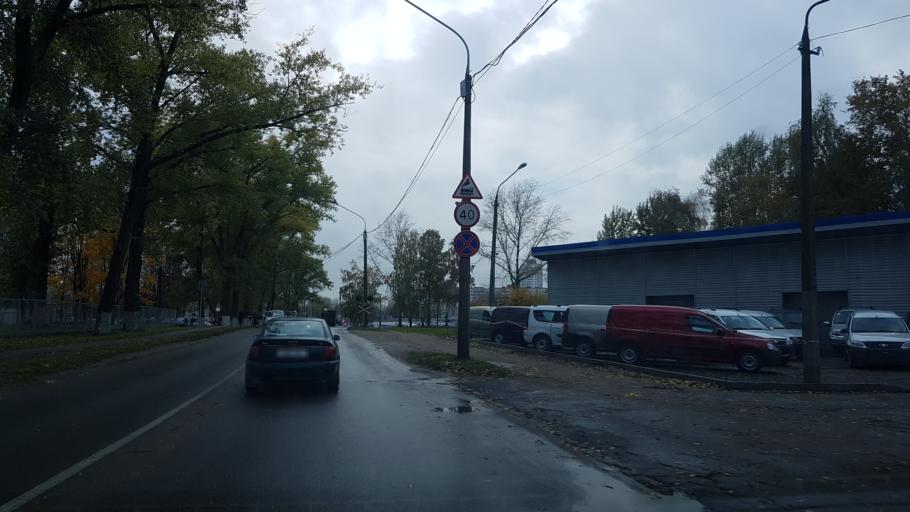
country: BY
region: Minsk
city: Syenitsa
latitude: 53.8433
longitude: 27.5437
